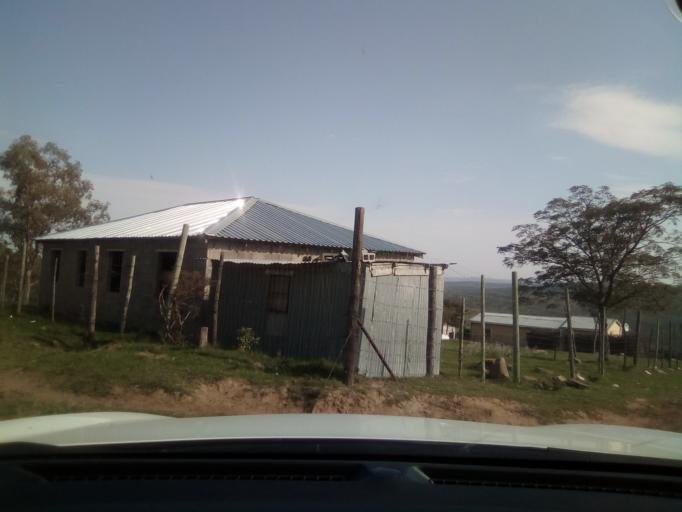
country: ZA
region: Eastern Cape
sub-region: Buffalo City Metropolitan Municipality
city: Bhisho
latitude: -32.9844
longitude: 27.2586
